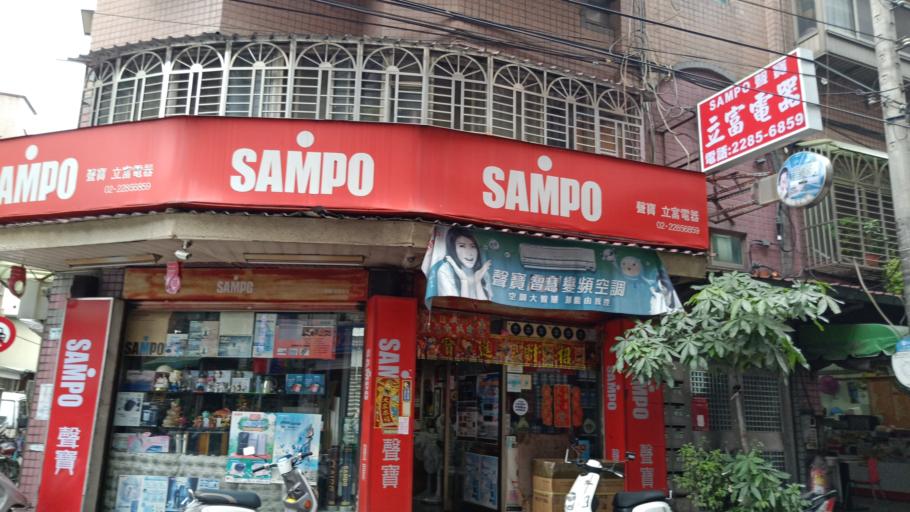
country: TW
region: Taipei
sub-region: Taipei
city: Banqiao
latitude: 25.0894
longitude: 121.4583
